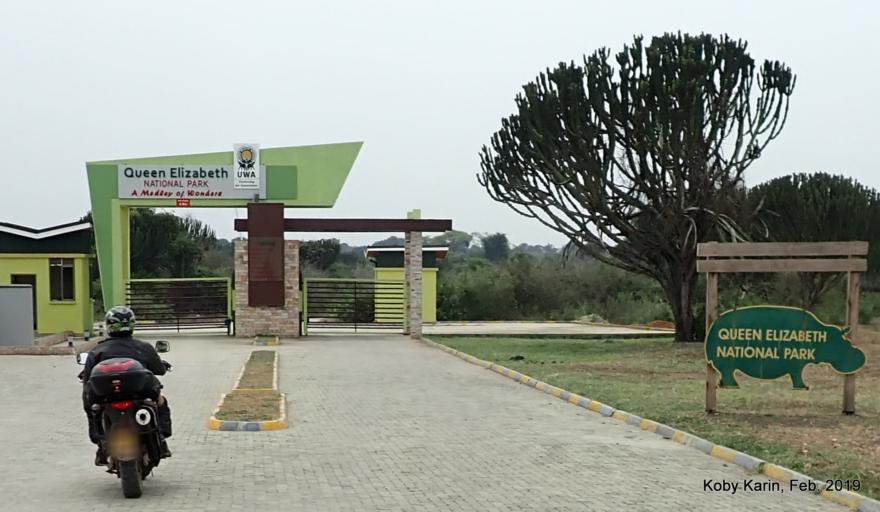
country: UG
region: Western Region
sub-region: Rubirizi District
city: Rubirizi
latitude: -0.1355
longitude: 29.9284
